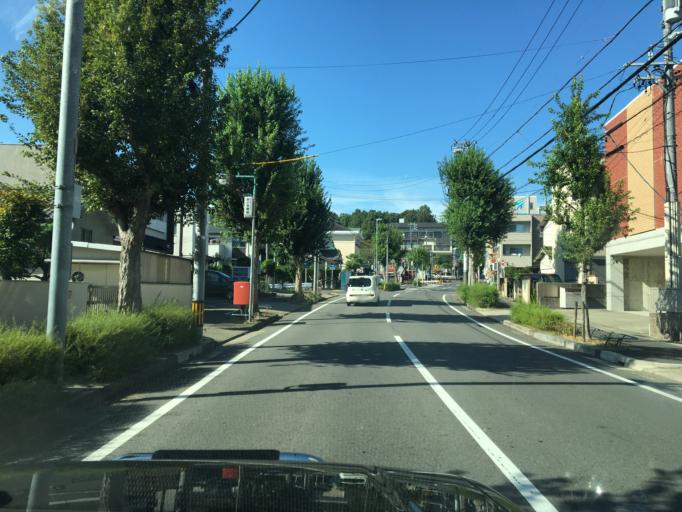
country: JP
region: Aichi
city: Kasugai
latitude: 35.2058
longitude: 136.9962
